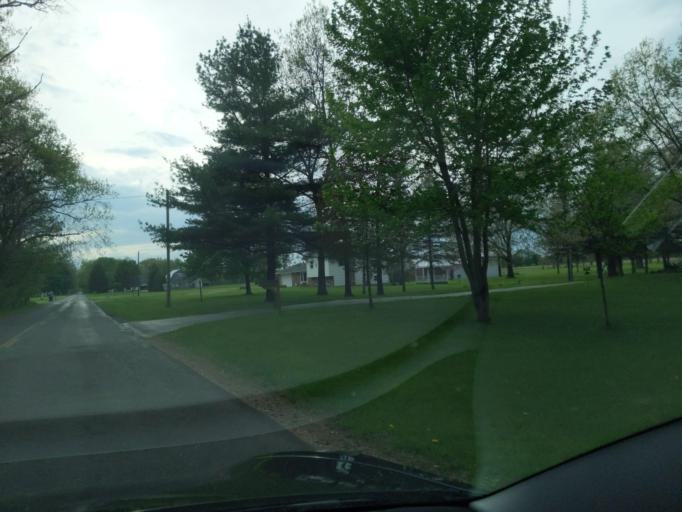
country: US
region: Michigan
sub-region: Ingham County
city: Stockbridge
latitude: 42.4392
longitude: -84.1556
